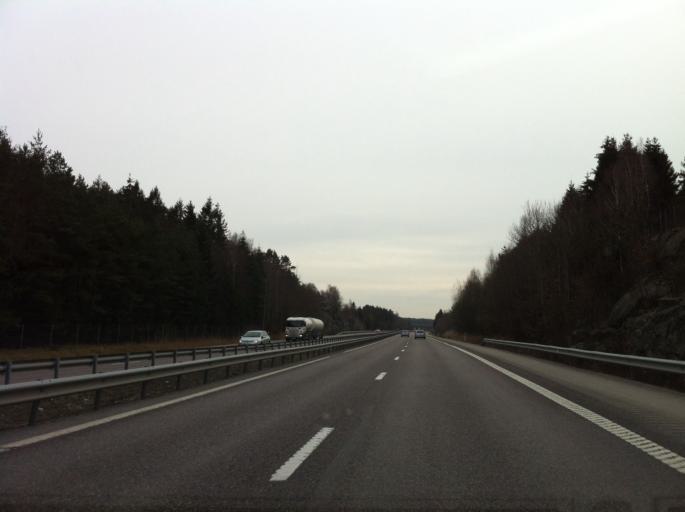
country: SE
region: Vaestra Goetaland
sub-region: Stenungsunds Kommun
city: Stora Hoga
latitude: 58.0183
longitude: 11.8436
